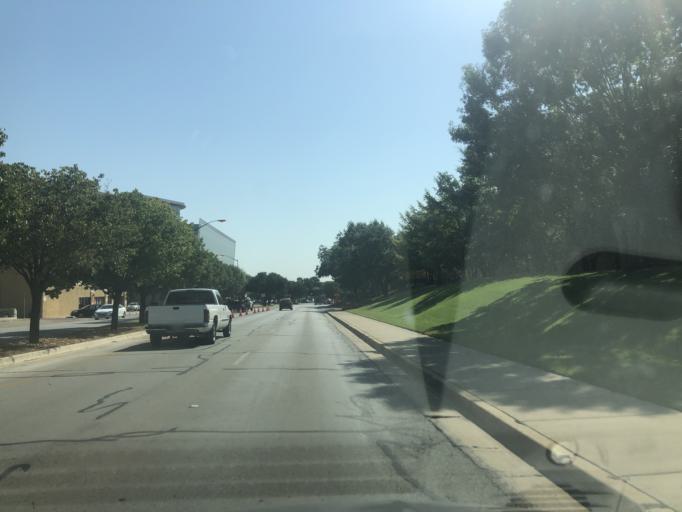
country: US
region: Texas
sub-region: Tarrant County
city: River Oaks
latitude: 32.7501
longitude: -97.3641
